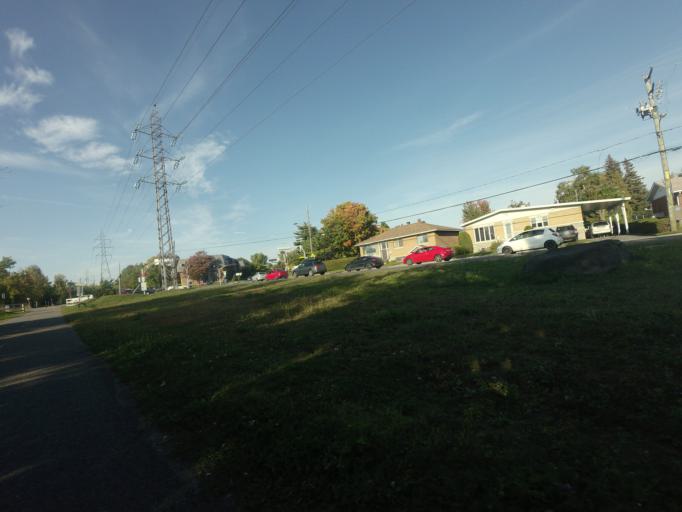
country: CA
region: Quebec
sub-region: Laurentides
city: Saint-Jerome
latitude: 45.7870
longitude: -73.9967
